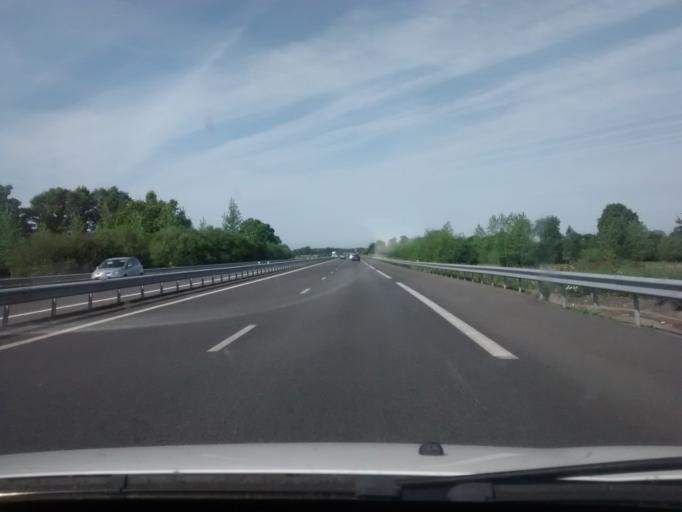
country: FR
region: Brittany
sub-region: Departement d'Ille-et-Vilaine
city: Romagne
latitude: 48.3556
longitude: -1.2562
